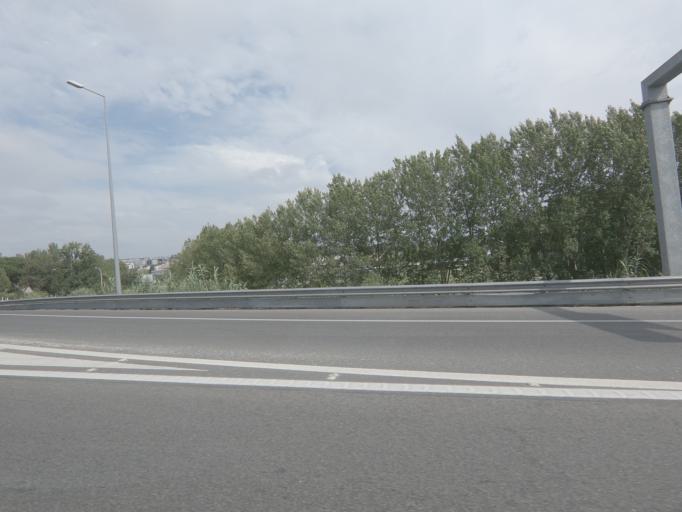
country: PT
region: Leiria
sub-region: Leiria
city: Leiria
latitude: 39.7525
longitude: -8.8169
